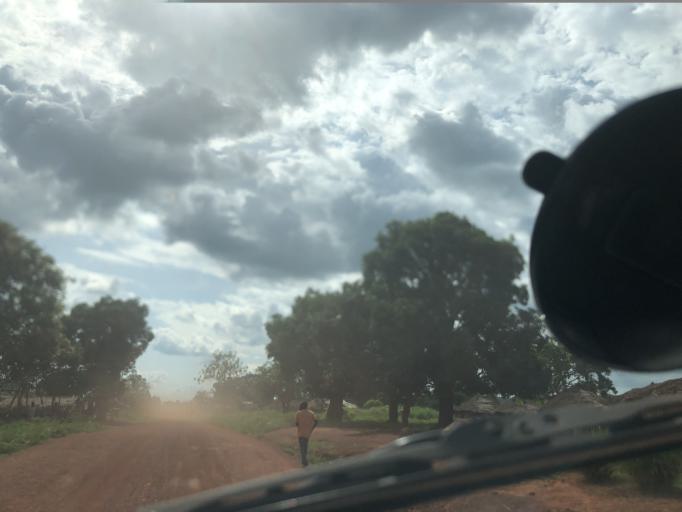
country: CF
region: Bangui
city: Bangui
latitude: 4.2022
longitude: 18.7206
